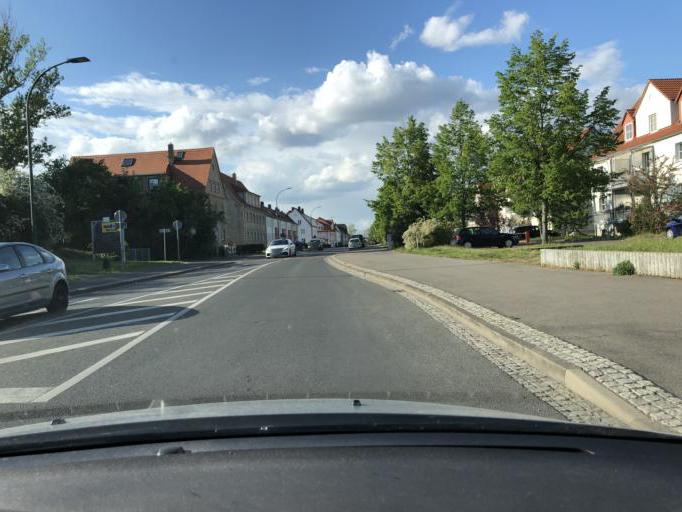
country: DE
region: Saxony
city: Markkleeberg
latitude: 51.2622
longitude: 12.3777
